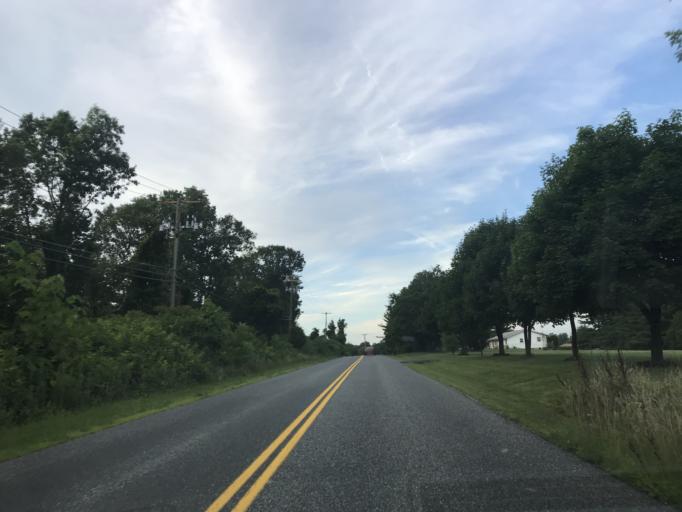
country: US
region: Maryland
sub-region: Harford County
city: Aberdeen
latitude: 39.5132
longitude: -76.2057
